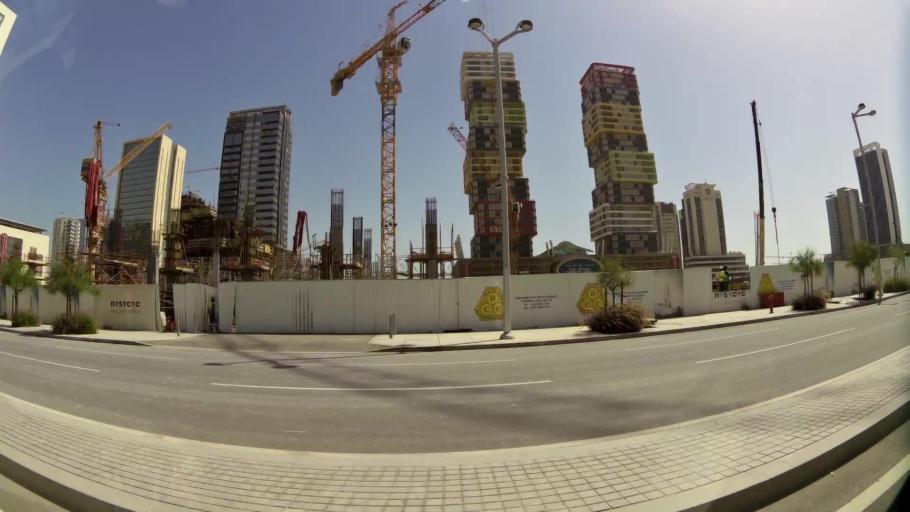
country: QA
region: Baladiyat ad Dawhah
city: Doha
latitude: 25.3871
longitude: 51.5209
